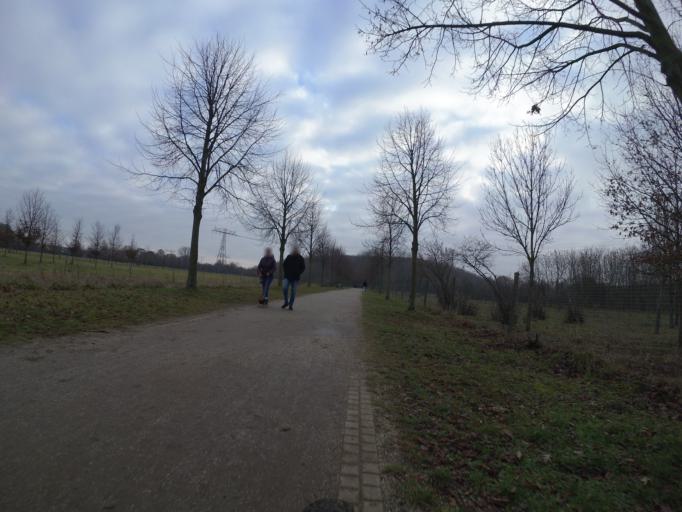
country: DE
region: Brandenburg
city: Ahrensfelde
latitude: 52.5618
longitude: 13.5814
